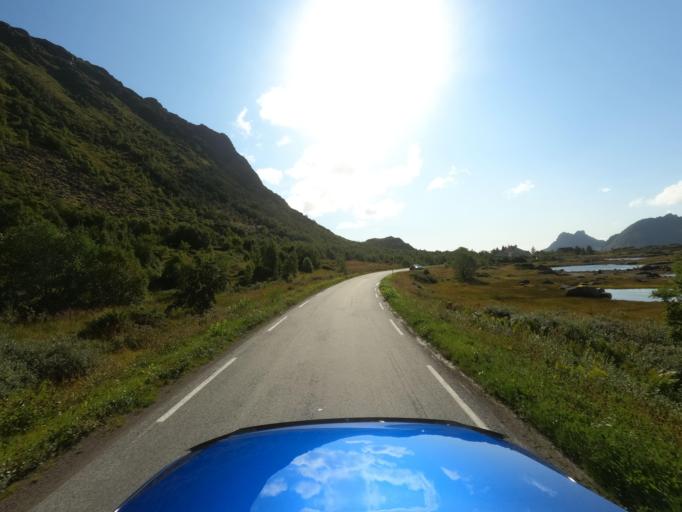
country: NO
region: Nordland
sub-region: Vestvagoy
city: Evjen
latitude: 68.1344
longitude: 13.7812
